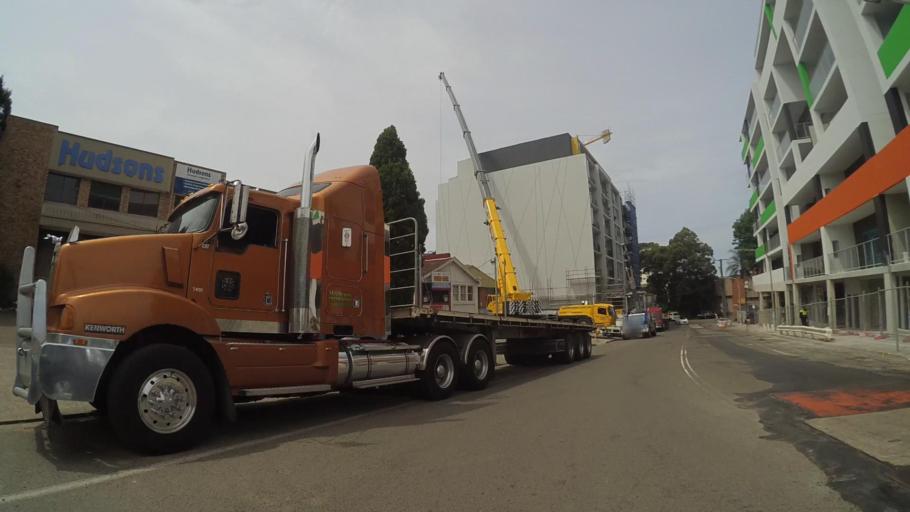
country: AU
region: New South Wales
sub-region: Rockdale
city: Arncliffe
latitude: -33.9323
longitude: 151.1498
